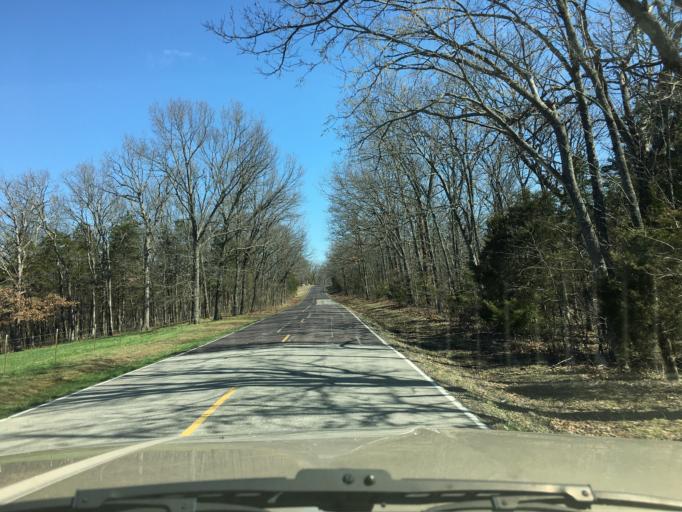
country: US
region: Missouri
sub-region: Franklin County
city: Gerald
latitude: 38.5341
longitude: -91.3323
